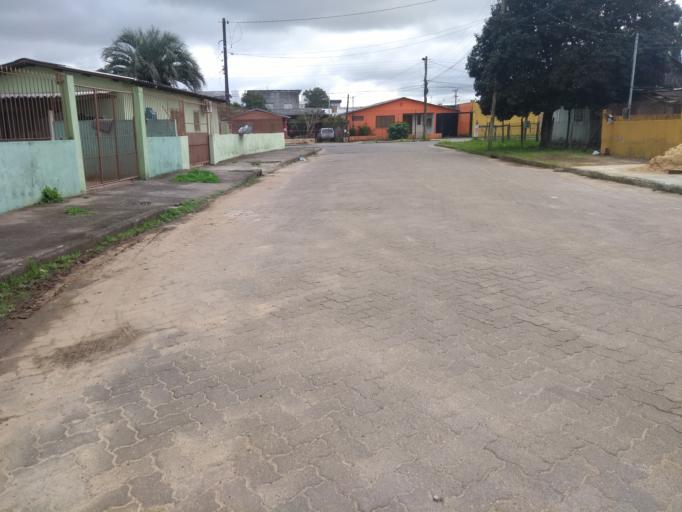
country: BR
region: Rio Grande do Sul
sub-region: Cachoeirinha
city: Cachoeirinha
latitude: -30.0027
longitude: -51.0766
